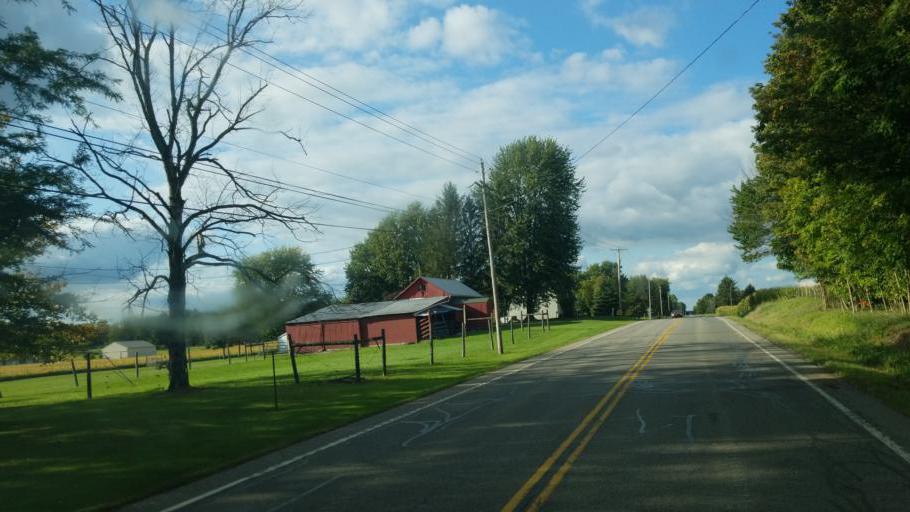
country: US
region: Ohio
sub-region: Richland County
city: Lincoln Heights
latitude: 40.8678
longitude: -82.5134
